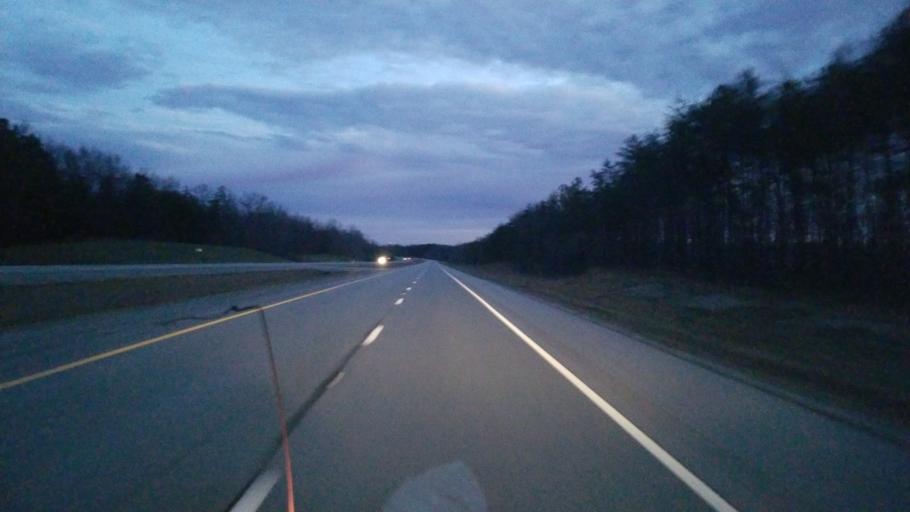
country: US
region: Tennessee
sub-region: Van Buren County
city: Spencer
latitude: 35.5927
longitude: -85.4699
